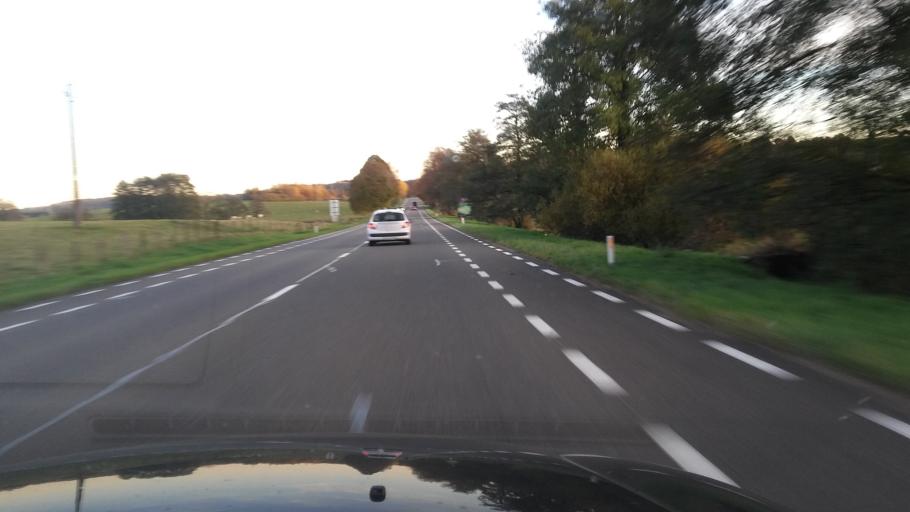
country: BE
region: Wallonia
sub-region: Province du Luxembourg
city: Herbeumont
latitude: 49.7246
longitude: 5.2409
